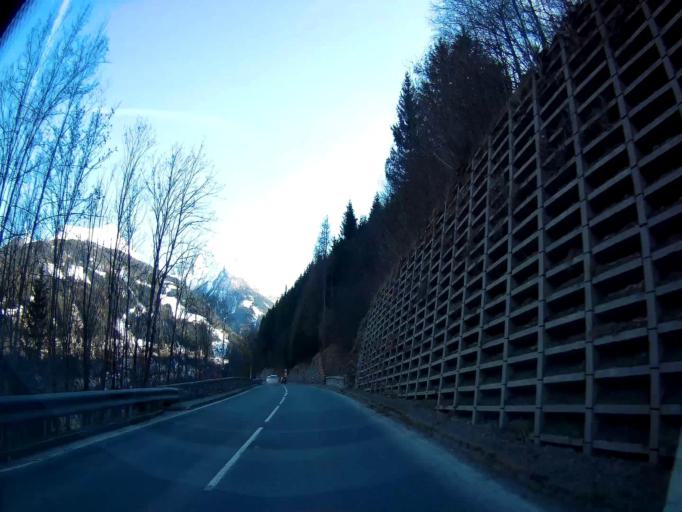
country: AT
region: Salzburg
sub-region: Politischer Bezirk Sankt Johann im Pongau
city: Bad Gastein
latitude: 47.1321
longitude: 13.1289
